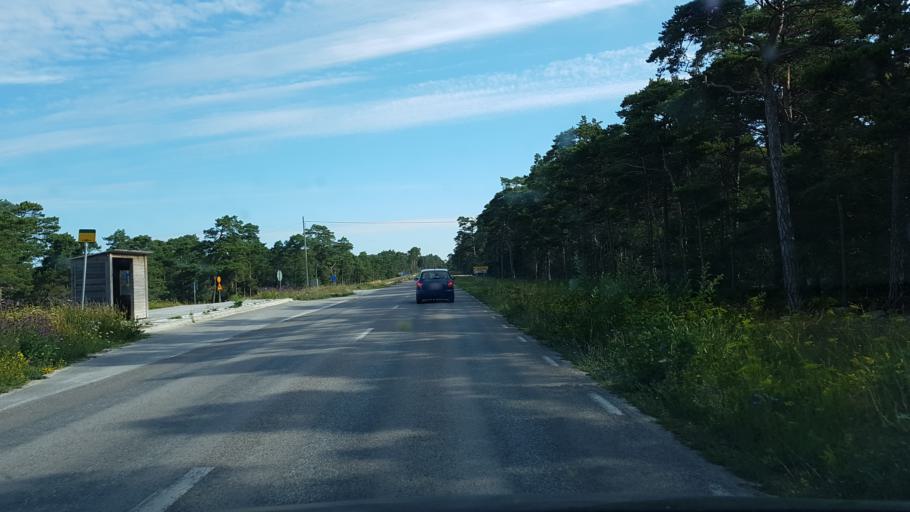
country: SE
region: Gotland
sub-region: Gotland
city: Visby
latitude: 57.7296
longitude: 18.4046
